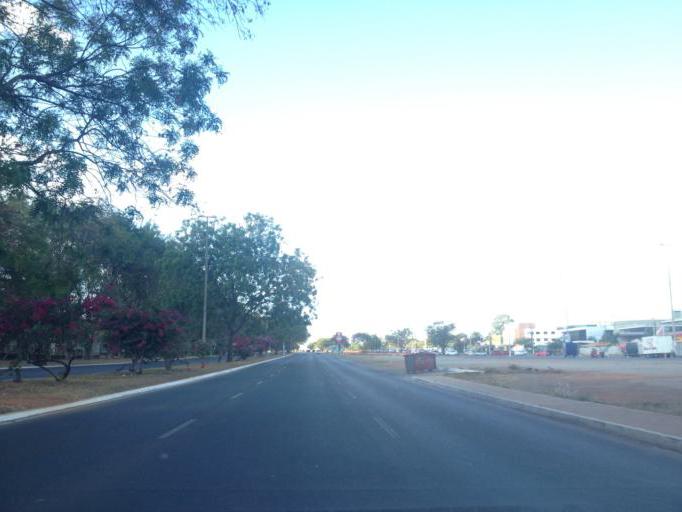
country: BR
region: Federal District
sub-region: Brasilia
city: Brasilia
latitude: -15.8348
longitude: -47.9143
